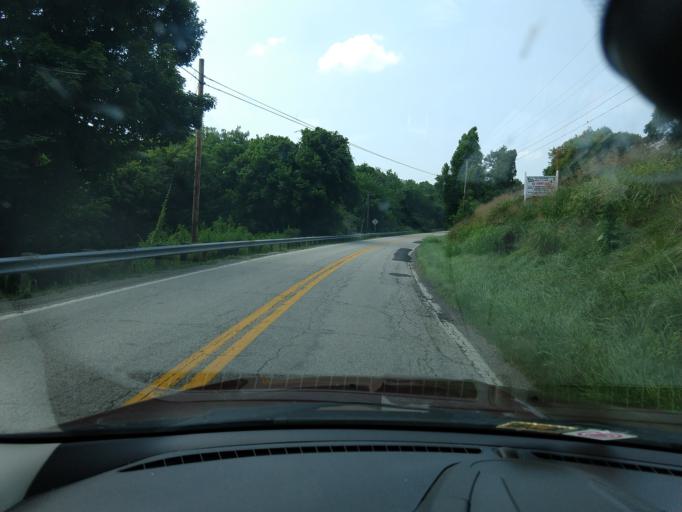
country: US
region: West Virginia
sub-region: Mason County
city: New Haven
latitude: 38.9251
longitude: -81.9127
